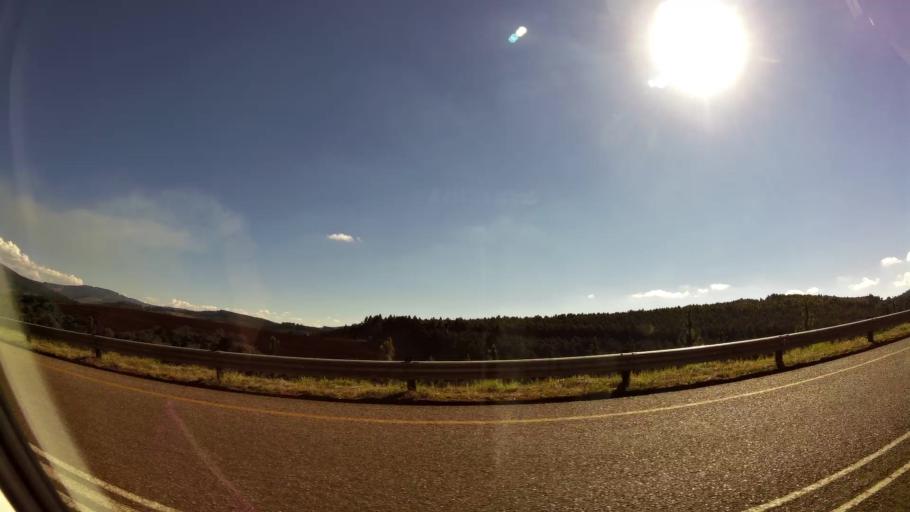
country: ZA
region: Limpopo
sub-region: Capricorn District Municipality
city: Mankoeng
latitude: -23.9300
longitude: 29.9572
